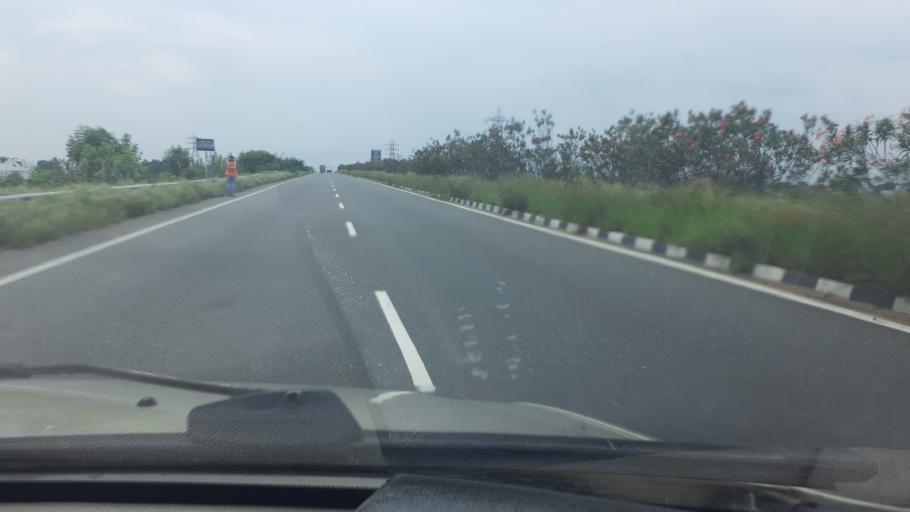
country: IN
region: Tamil Nadu
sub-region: Madurai
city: Tirupparangunram
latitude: 9.8362
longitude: 77.9834
